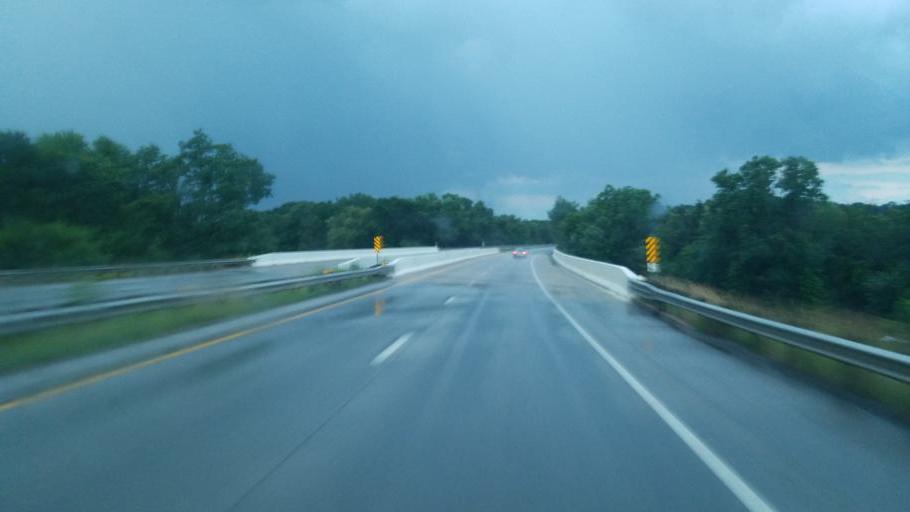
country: US
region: Ohio
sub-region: Summit County
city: Clinton
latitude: 40.9268
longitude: -81.6490
